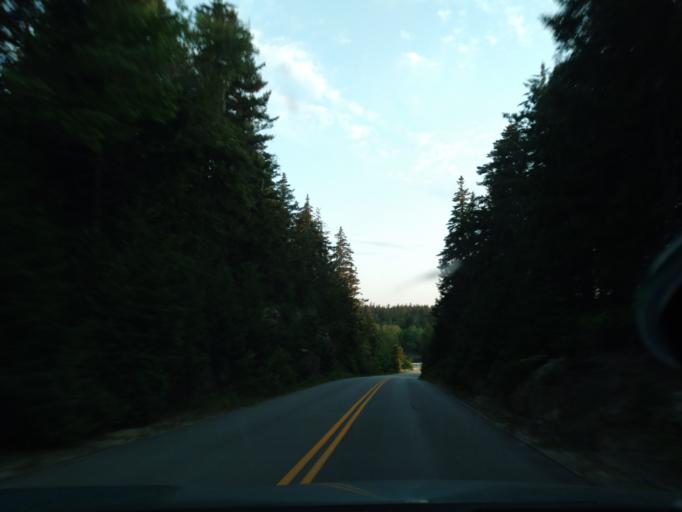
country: US
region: Maine
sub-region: Hancock County
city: Gouldsboro
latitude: 44.3767
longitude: -68.0695
